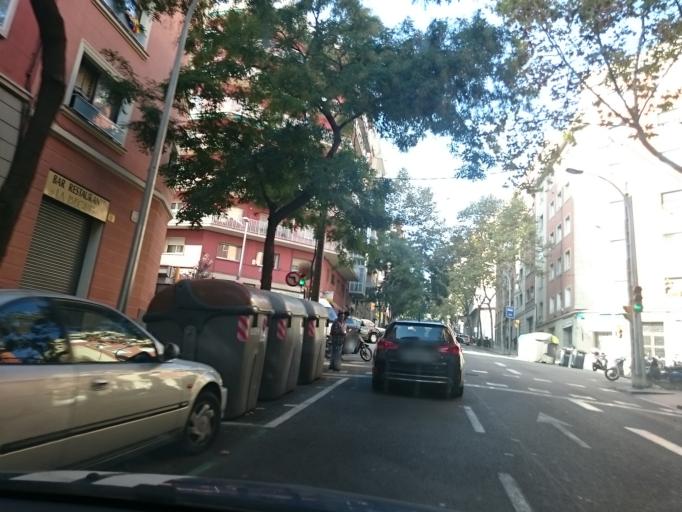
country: ES
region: Catalonia
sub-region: Provincia de Barcelona
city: Horta-Guinardo
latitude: 41.4108
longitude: 2.1705
